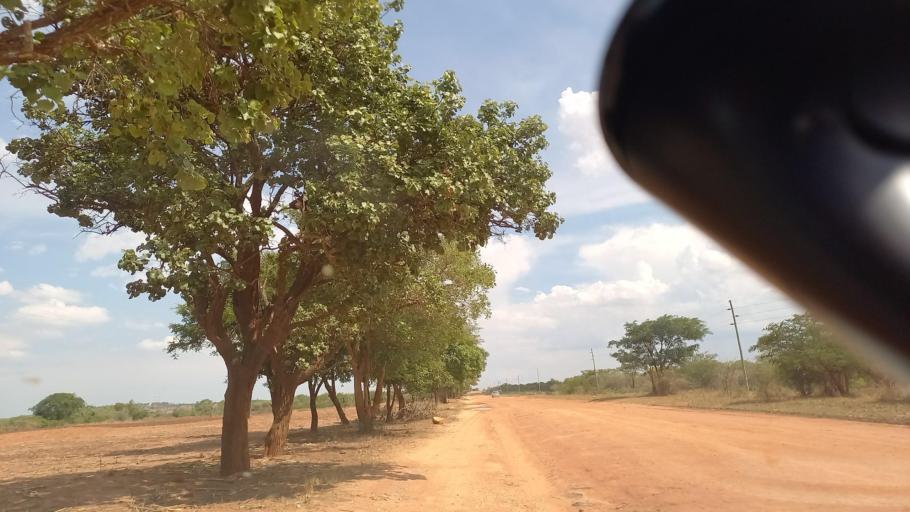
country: ZM
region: Lusaka
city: Kafue
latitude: -16.1379
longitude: 28.0517
